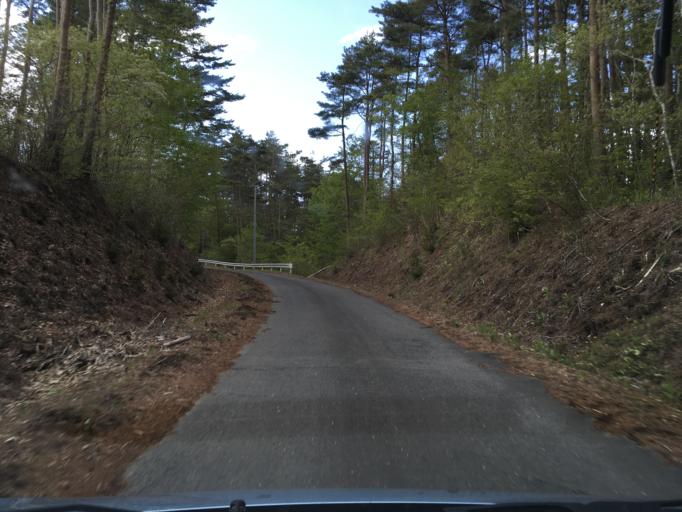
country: JP
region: Iwate
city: Ichinoseki
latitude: 38.7970
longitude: 141.4138
